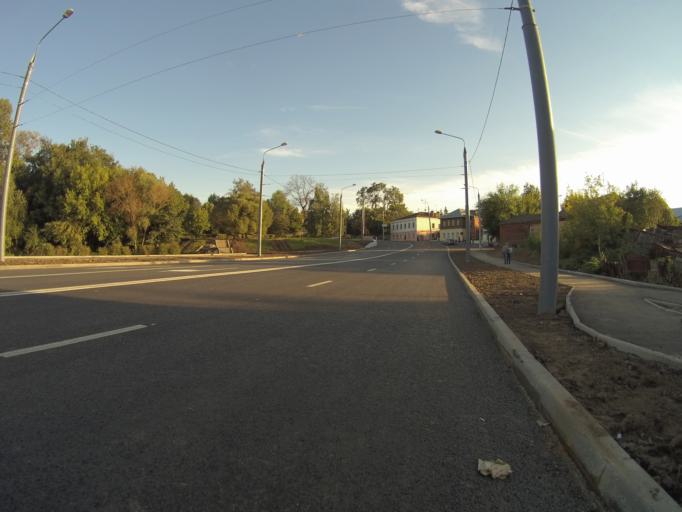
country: RU
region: Vladimir
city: Vladimir
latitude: 56.1336
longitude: 40.4022
